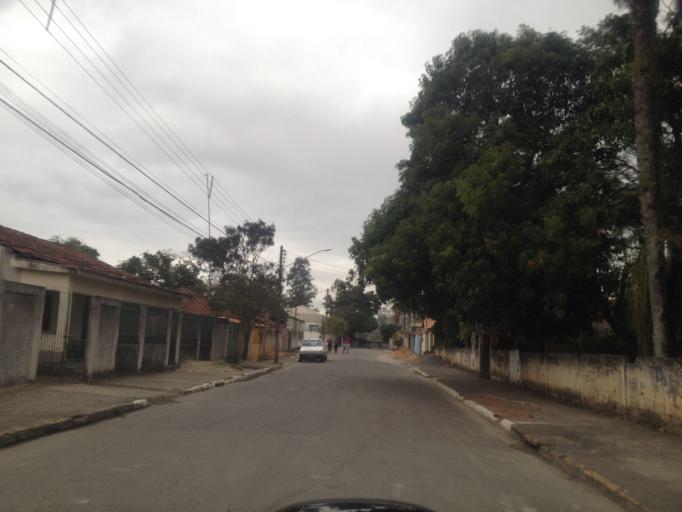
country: BR
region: Rio de Janeiro
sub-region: Porto Real
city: Porto Real
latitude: -22.4113
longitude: -44.2971
